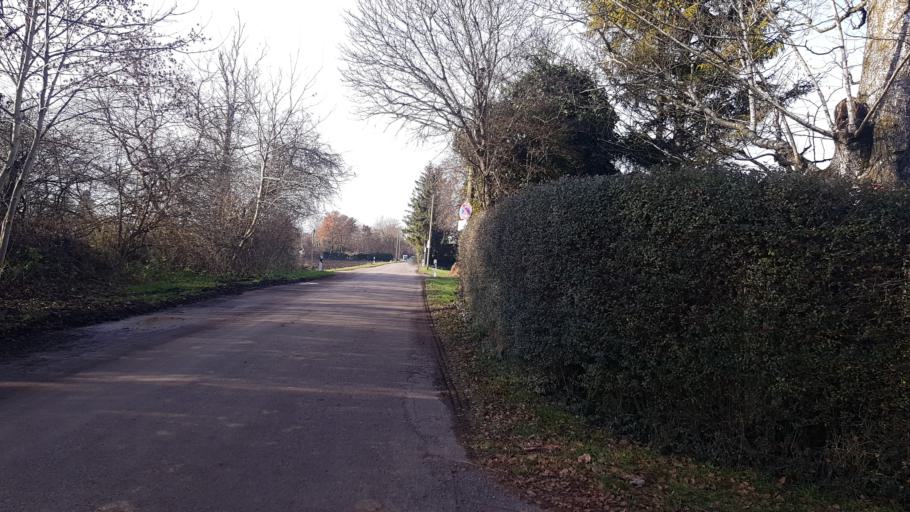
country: DE
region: Bavaria
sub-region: Upper Bavaria
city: Karlsfeld
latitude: 48.2427
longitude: 11.5114
